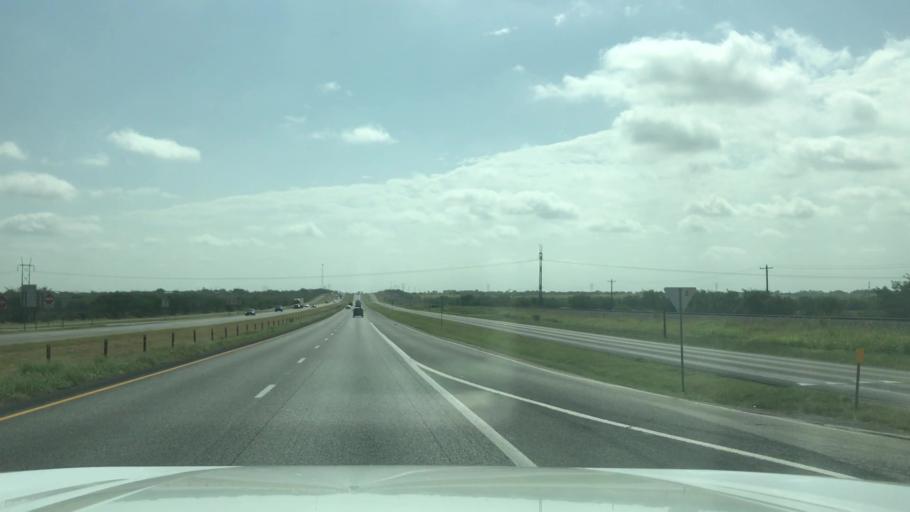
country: US
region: Texas
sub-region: Taylor County
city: Tye
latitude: 32.4588
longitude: -99.9165
